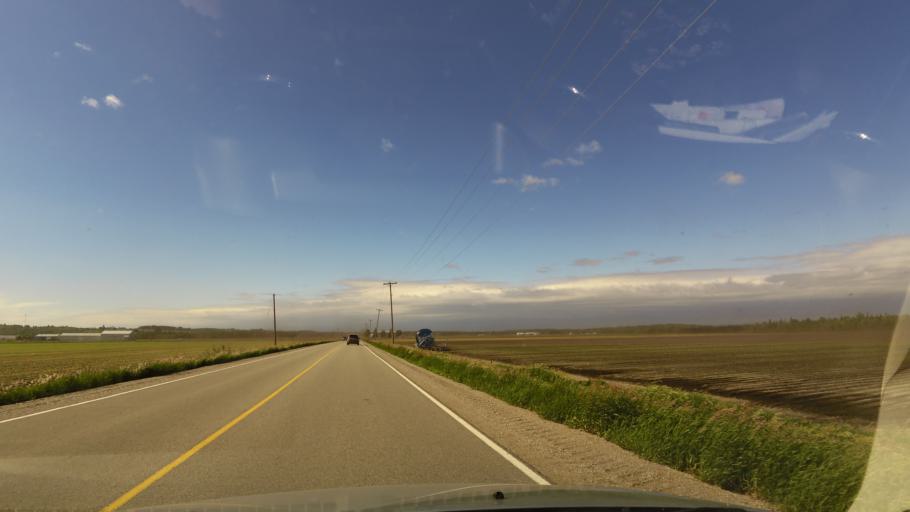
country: CA
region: Ontario
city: Innisfil
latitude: 44.2141
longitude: -79.6301
